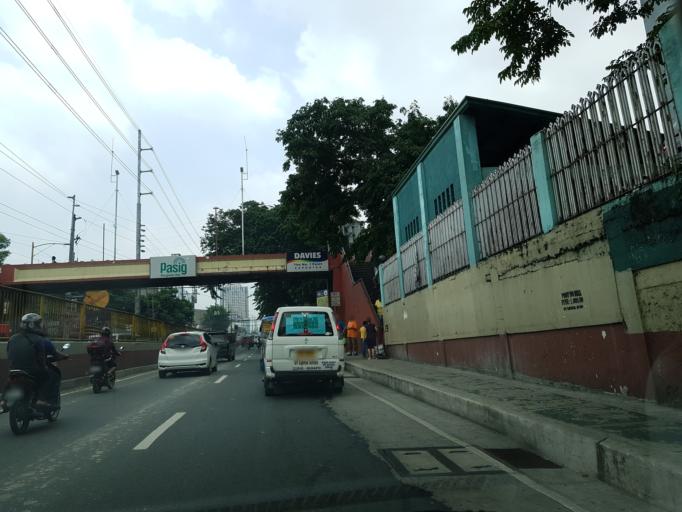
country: PH
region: Metro Manila
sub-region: Pasig
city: Pasig City
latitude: 14.5637
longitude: 121.0655
